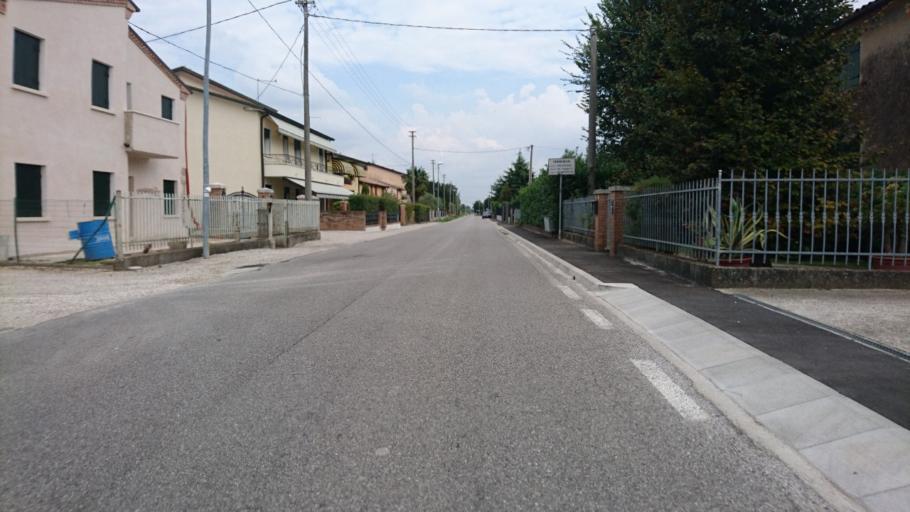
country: IT
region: Veneto
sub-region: Provincia di Padova
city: Cervarese Santa Croce
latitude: 45.4397
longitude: 11.6963
